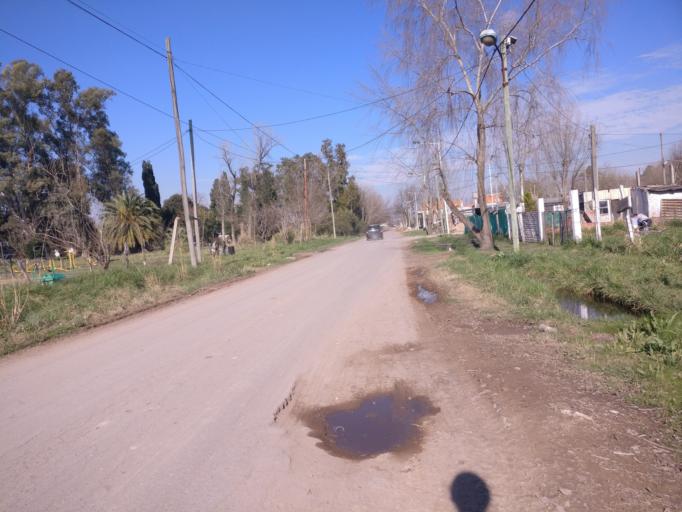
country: AR
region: Buenos Aires
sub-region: Partido de Ezeiza
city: Ezeiza
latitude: -34.9341
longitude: -58.6135
